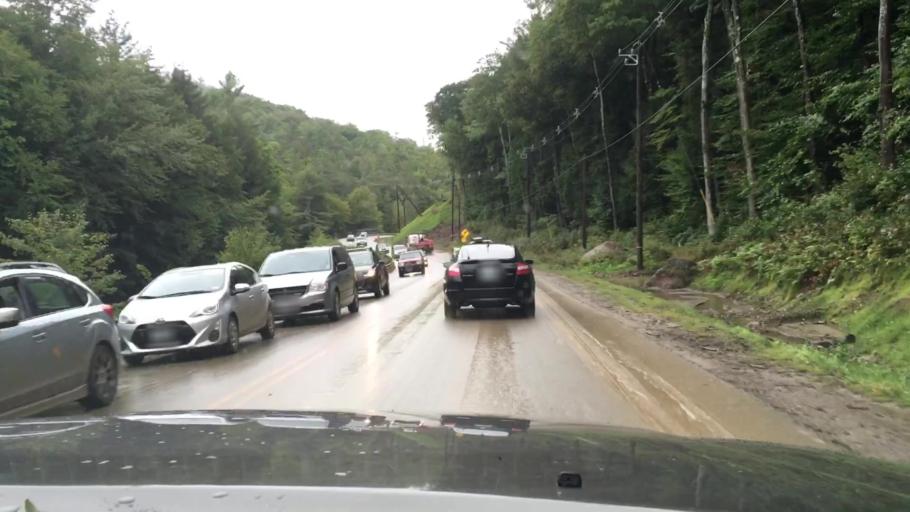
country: US
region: New Hampshire
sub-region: Cheshire County
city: Marlborough
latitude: 42.9894
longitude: -72.1976
